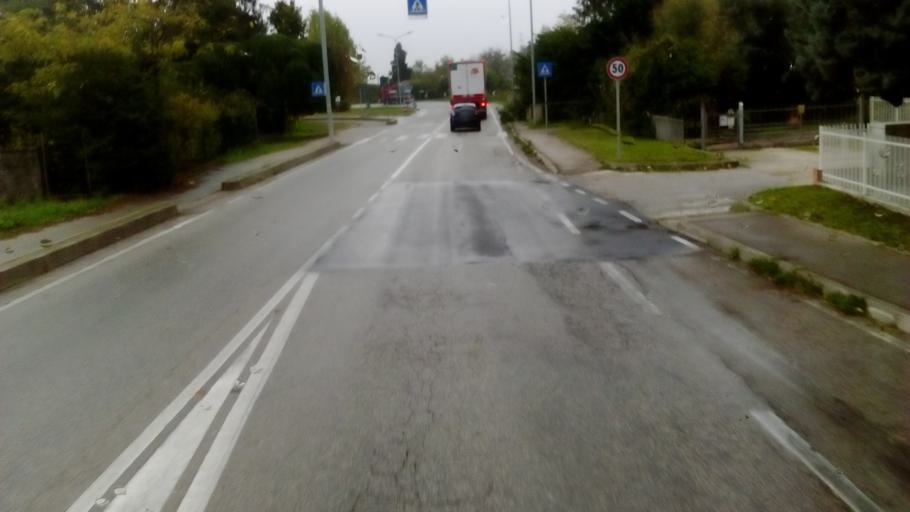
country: IT
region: Veneto
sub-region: Provincia di Vicenza
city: Breganze
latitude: 45.6904
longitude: 11.5626
